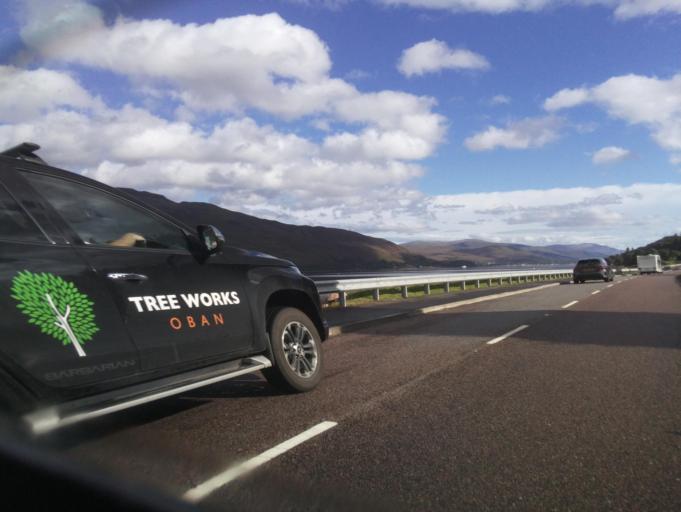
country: GB
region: Scotland
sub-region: Highland
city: Fort William
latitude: 56.7910
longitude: -5.1464
